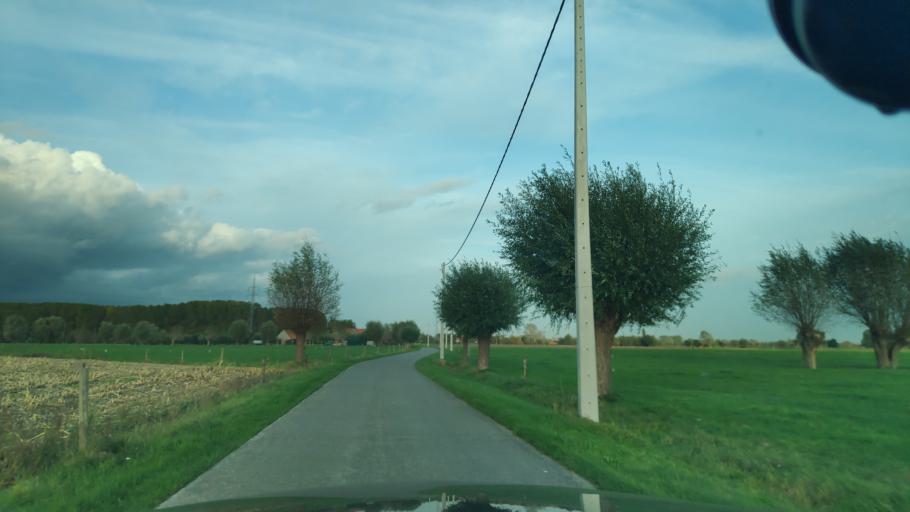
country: BE
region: Flanders
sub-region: Provincie Oost-Vlaanderen
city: Aalter
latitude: 51.1109
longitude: 3.4832
